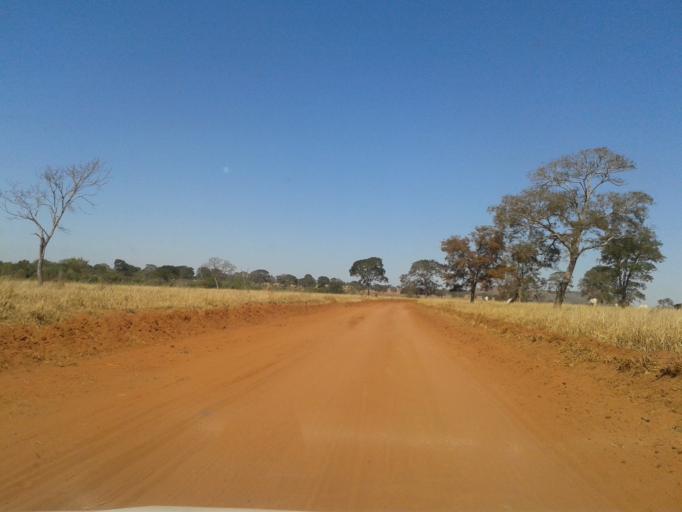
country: BR
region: Minas Gerais
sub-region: Santa Vitoria
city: Santa Vitoria
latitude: -19.1625
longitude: -50.1562
